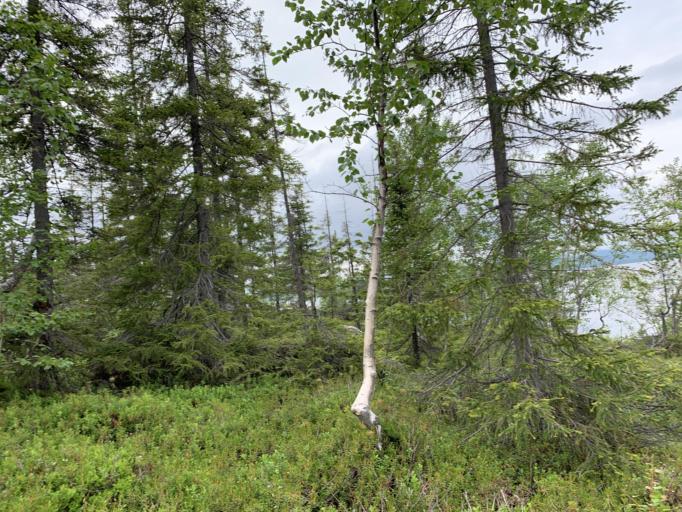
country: RU
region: Murmansk
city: Monchegorsk
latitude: 67.7954
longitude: 33.0522
